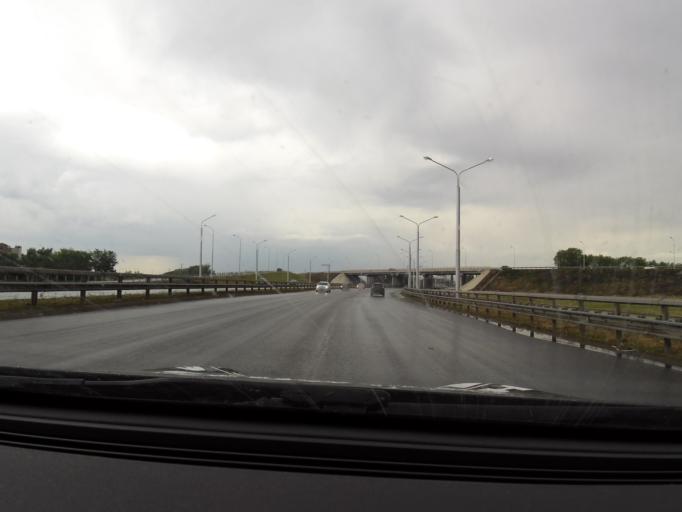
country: RU
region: Bashkortostan
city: Mikhaylovka
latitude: 54.7984
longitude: 55.8687
